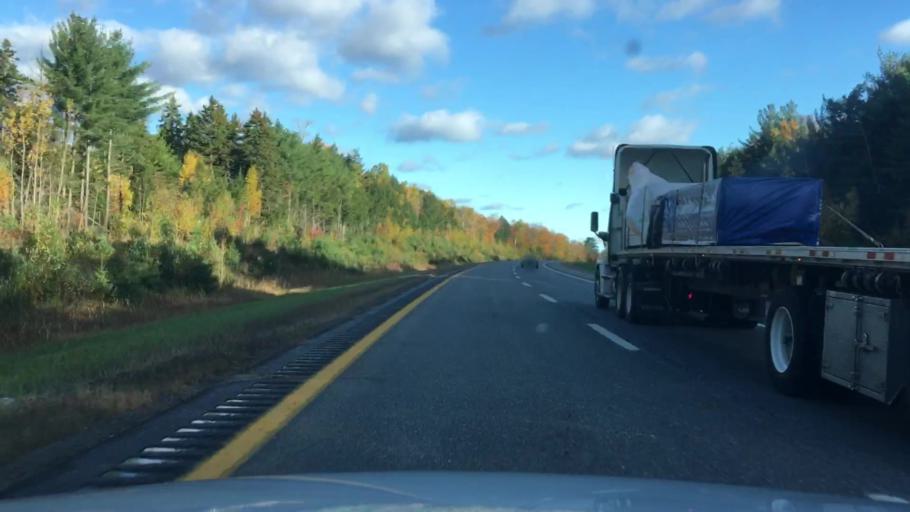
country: US
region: Maine
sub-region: Penobscot County
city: Greenbush
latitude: 45.1520
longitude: -68.7039
